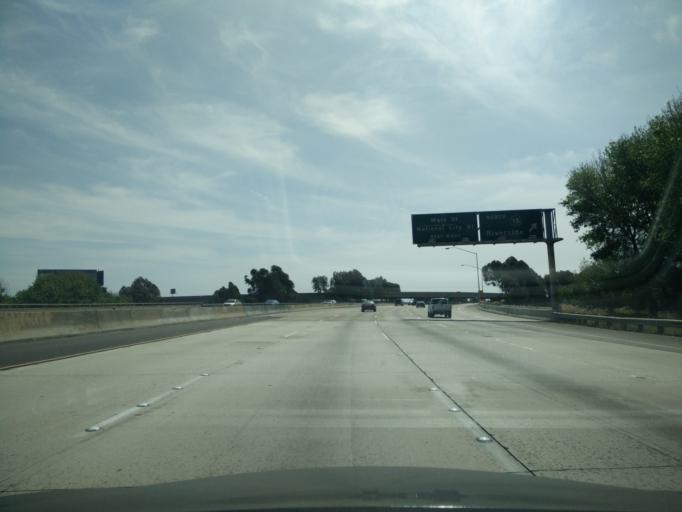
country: US
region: California
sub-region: San Diego County
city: National City
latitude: 32.6939
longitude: -117.1239
